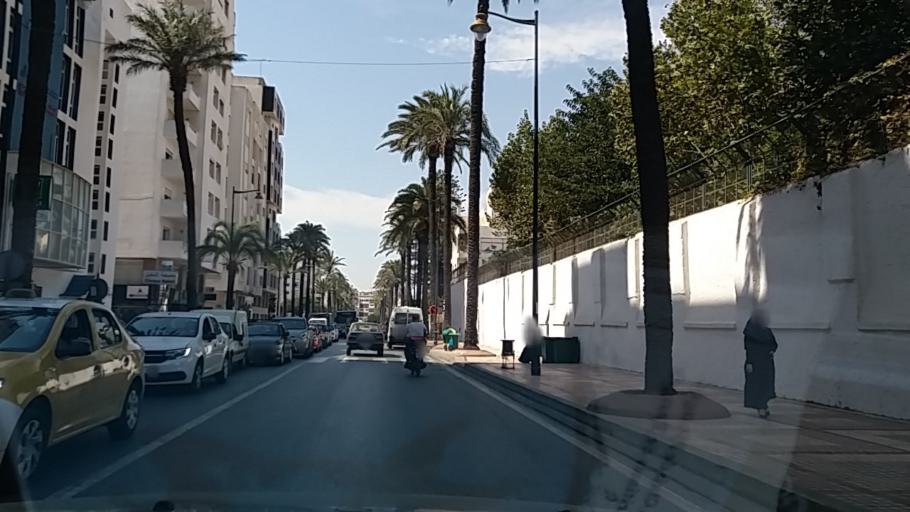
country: MA
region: Tanger-Tetouan
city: Tetouan
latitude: 35.5690
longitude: -5.3811
